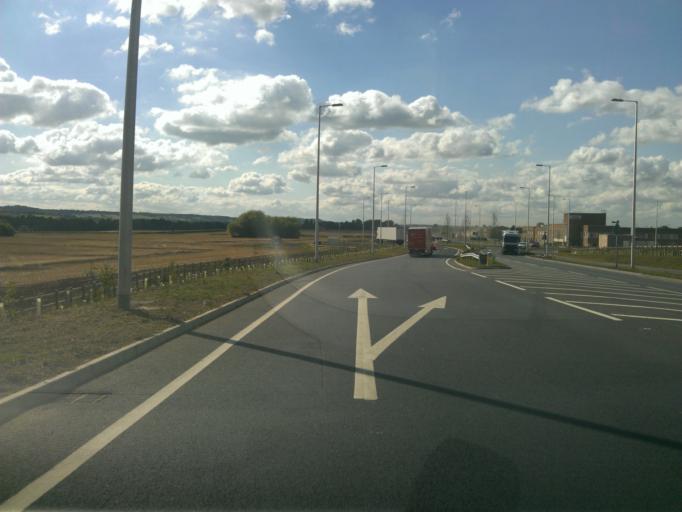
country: GB
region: England
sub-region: Warwickshire
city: Nuneaton
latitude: 52.5521
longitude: -1.4615
